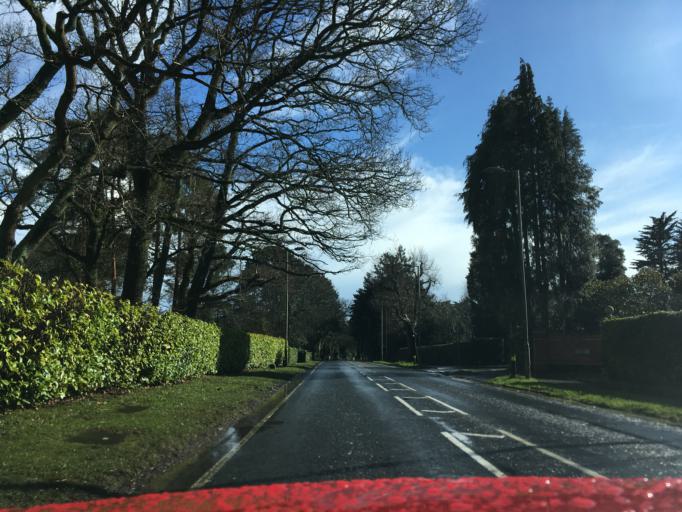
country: GB
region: England
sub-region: Southampton
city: Southampton
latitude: 50.9594
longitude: -1.4058
